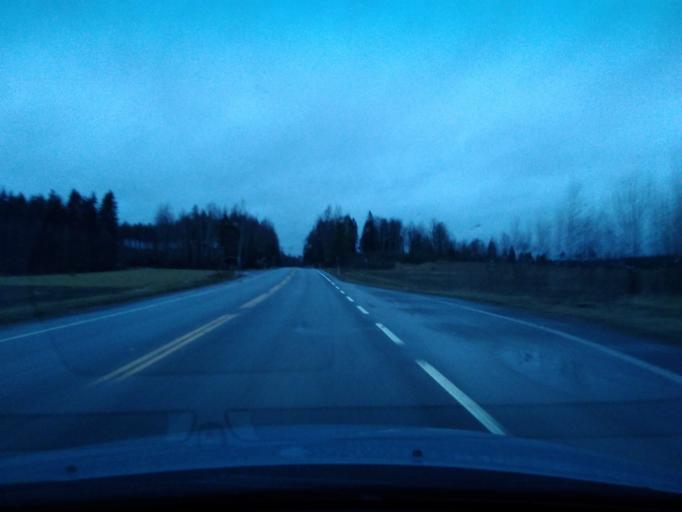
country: FI
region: Uusimaa
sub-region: Porvoo
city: Porvoo
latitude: 60.4034
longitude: 25.5919
